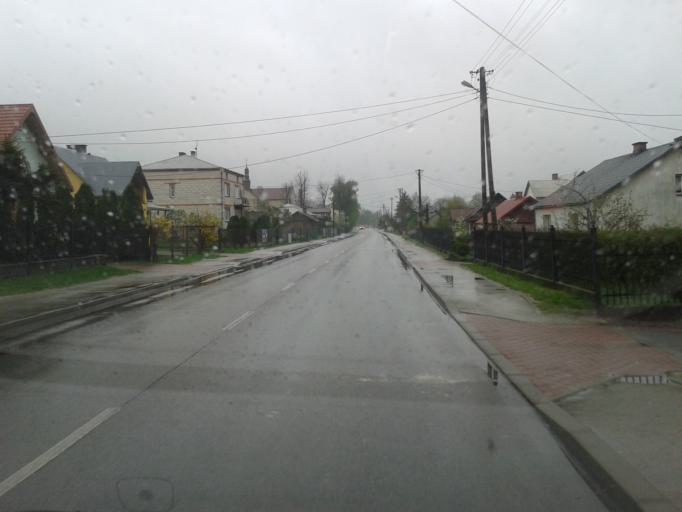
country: PL
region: Lublin Voivodeship
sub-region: Powiat tomaszowski
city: Belzec
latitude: 50.3837
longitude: 23.4308
